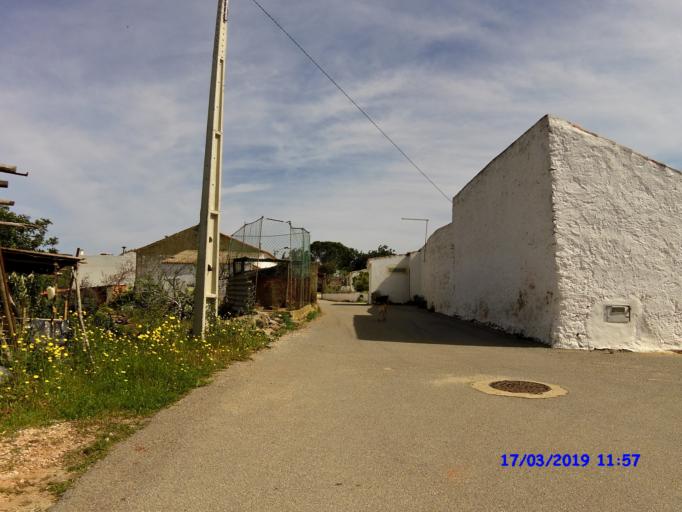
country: PT
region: Faro
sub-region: Silves
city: Sao Bartolomeu de Messines
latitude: 37.2534
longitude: -8.3489
